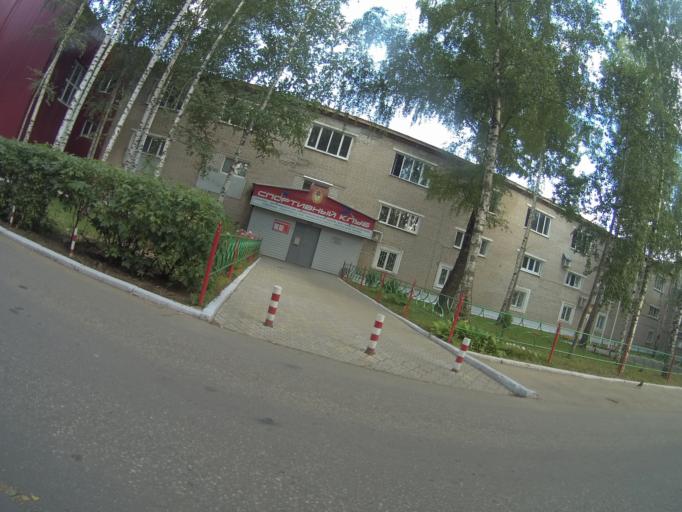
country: RU
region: Vladimir
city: Vladimir
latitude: 56.1346
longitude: 40.3614
